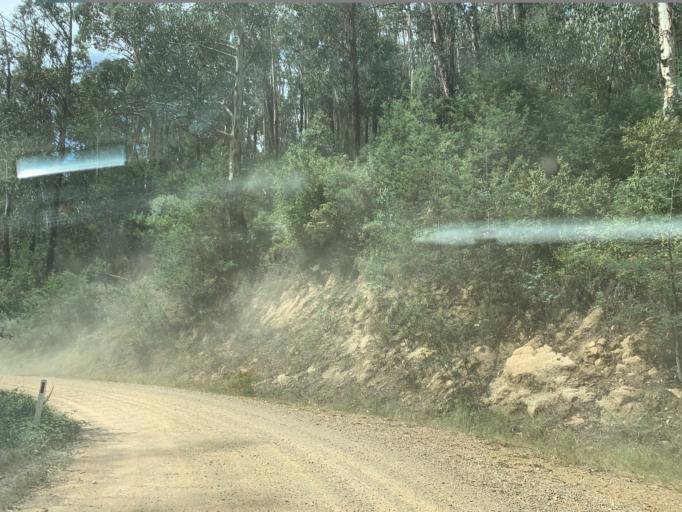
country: AU
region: Victoria
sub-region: Mansfield
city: Mansfield
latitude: -37.1008
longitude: 146.5104
